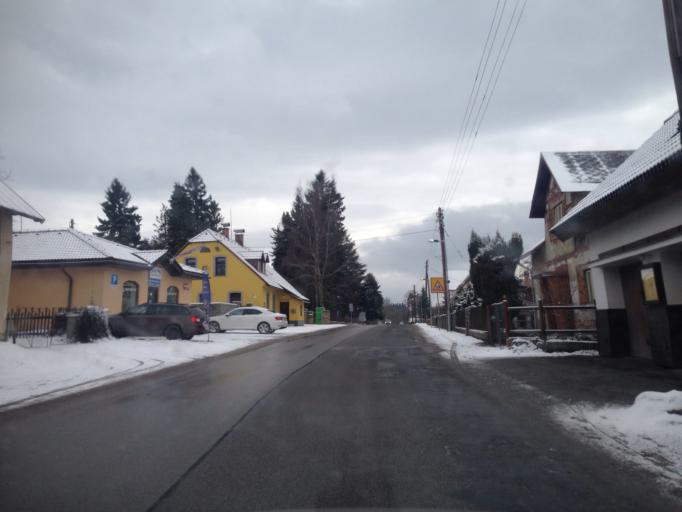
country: CZ
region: Liberecky
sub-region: Okres Semily
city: Vysoke nad Jizerou
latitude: 50.6874
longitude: 15.3992
